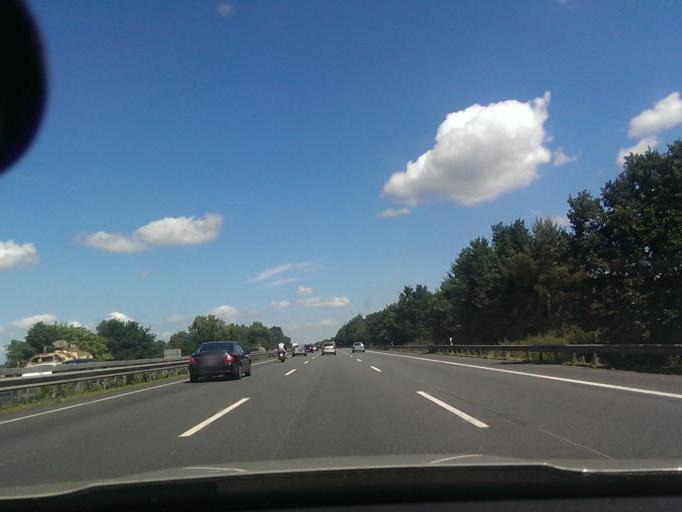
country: DE
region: Lower Saxony
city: Hademstorf
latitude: 52.7228
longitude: 9.6801
